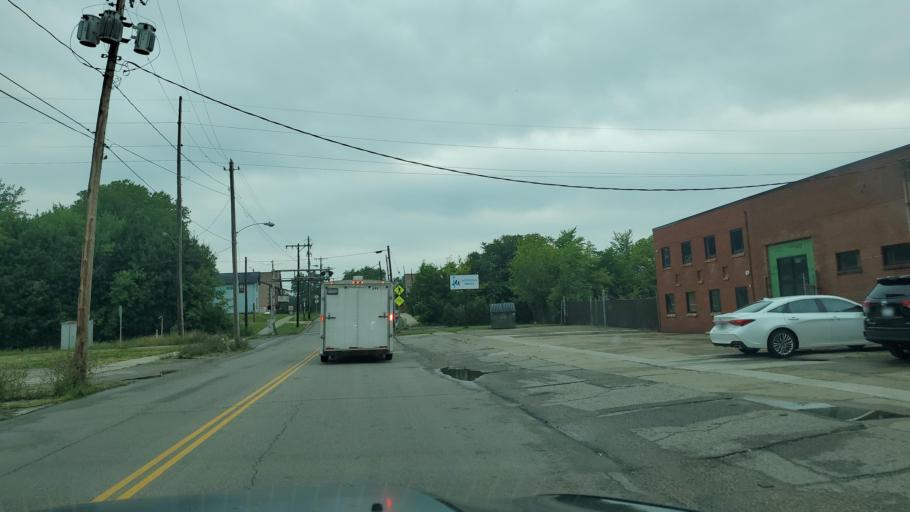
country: US
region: Ohio
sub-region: Trumbull County
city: Warren
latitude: 41.2412
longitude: -80.8069
